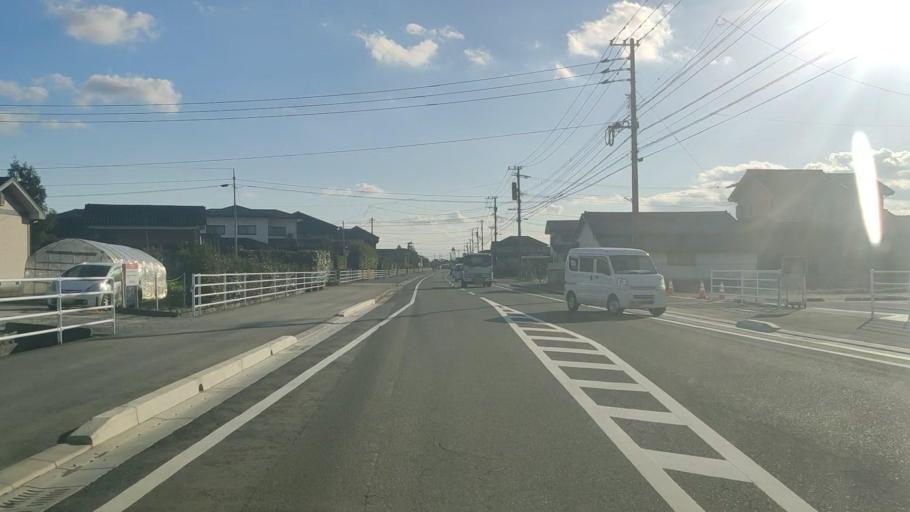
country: JP
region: Saga Prefecture
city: Saga-shi
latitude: 33.3157
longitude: 130.2663
